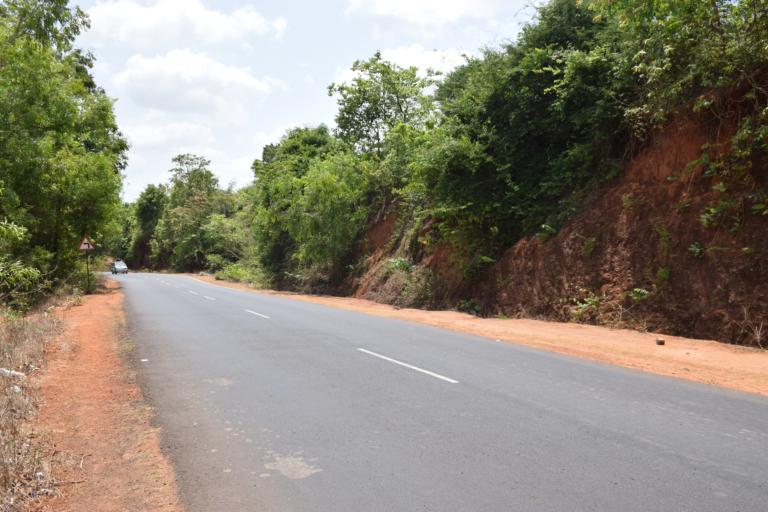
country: IN
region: Maharashtra
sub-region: Ratnagiri
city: Rajapur
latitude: 16.5833
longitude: 73.5927
